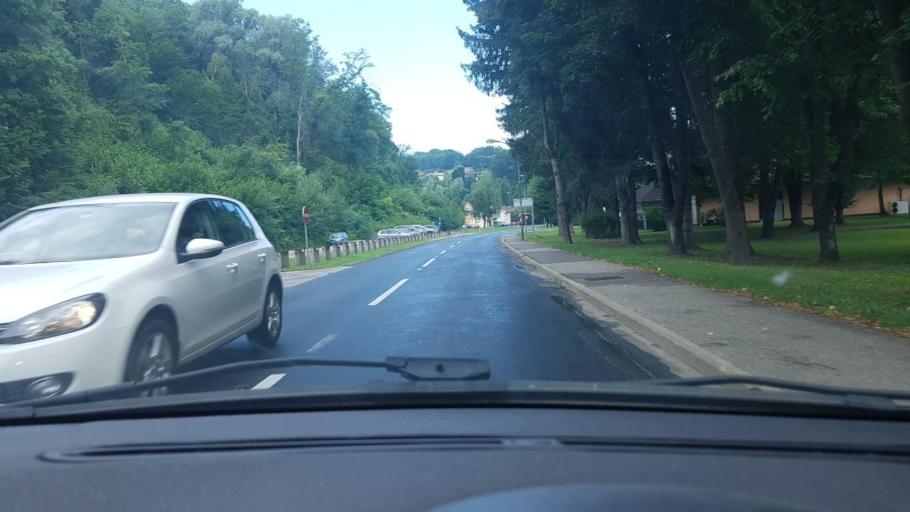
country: AT
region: Styria
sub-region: Politischer Bezirk Suedoststeiermark
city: Mureck
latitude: 46.6970
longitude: 15.7392
